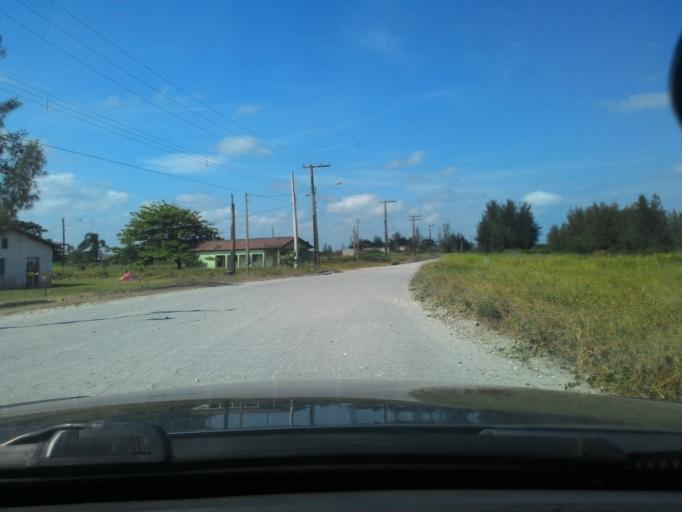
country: BR
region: Sao Paulo
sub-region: Iguape
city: Iguape
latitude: -24.8325
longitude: -47.6725
